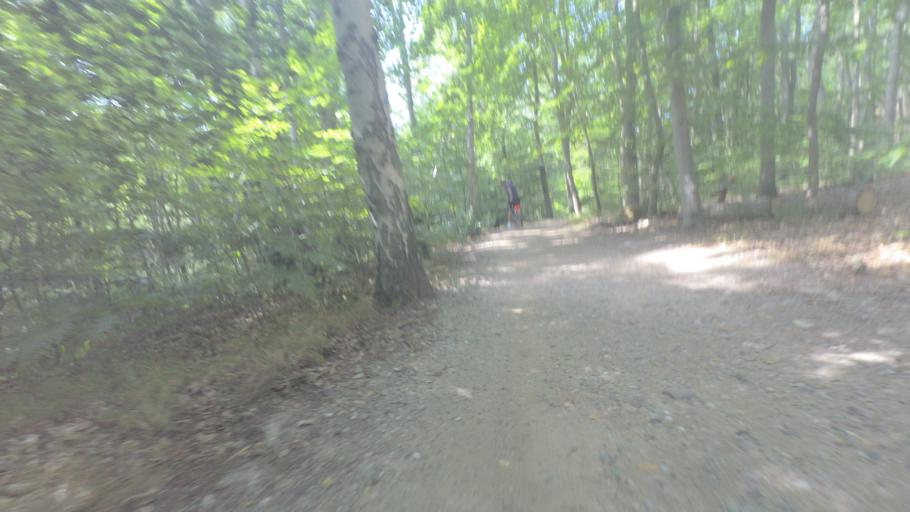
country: DE
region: Mecklenburg-Vorpommern
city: Klink
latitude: 53.5073
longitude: 12.6444
